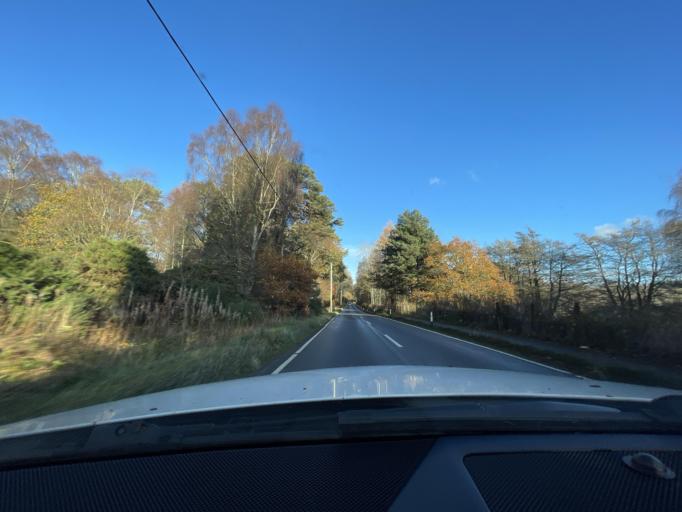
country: GB
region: Scotland
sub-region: Highland
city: Inverness
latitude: 57.4289
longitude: -4.2826
